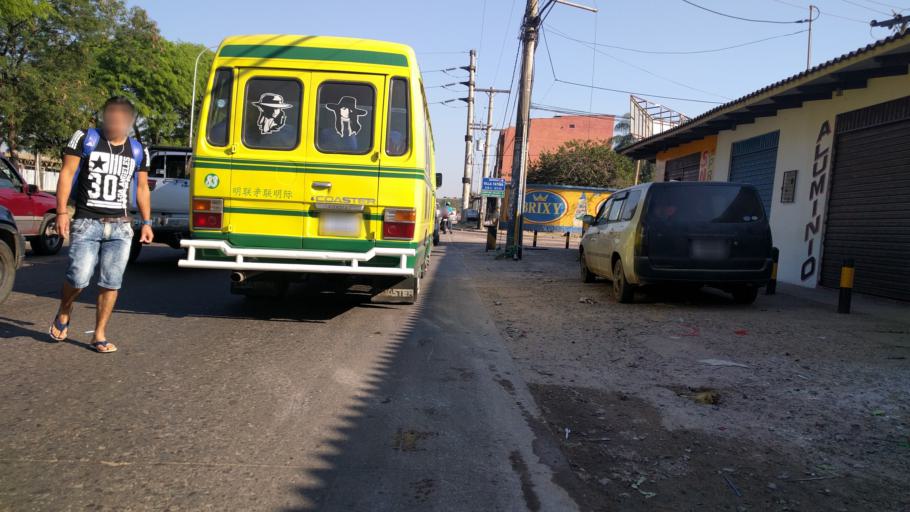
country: BO
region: Santa Cruz
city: Santa Cruz de la Sierra
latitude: -17.8133
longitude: -63.2064
